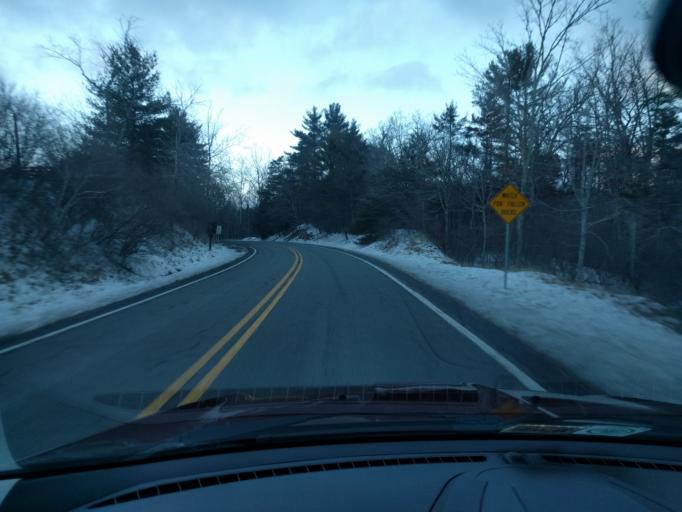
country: US
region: Virginia
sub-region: Bath County
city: Warm Springs
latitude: 38.0668
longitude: -79.8306
